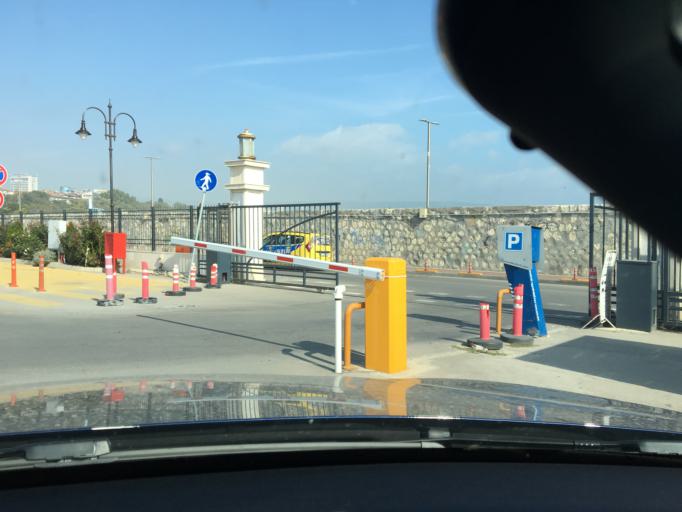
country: BG
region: Varna
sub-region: Obshtina Varna
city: Varna
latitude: 43.1955
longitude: 27.9211
